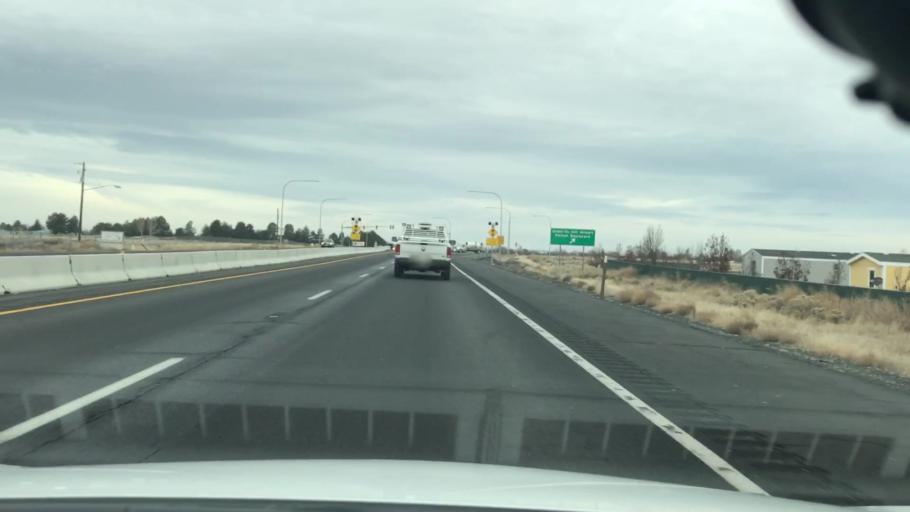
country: US
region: Washington
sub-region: Grant County
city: Cascade Valley
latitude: 47.1555
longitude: -119.3089
